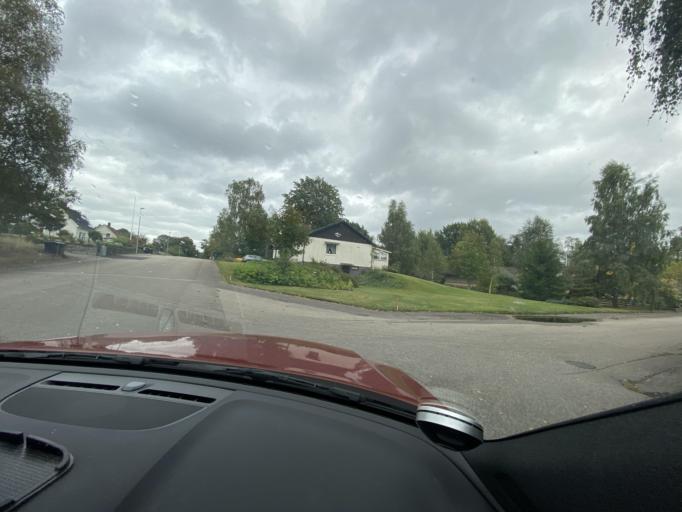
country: SE
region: Kronoberg
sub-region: Markaryds Kommun
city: Markaryd
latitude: 56.4606
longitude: 13.6158
